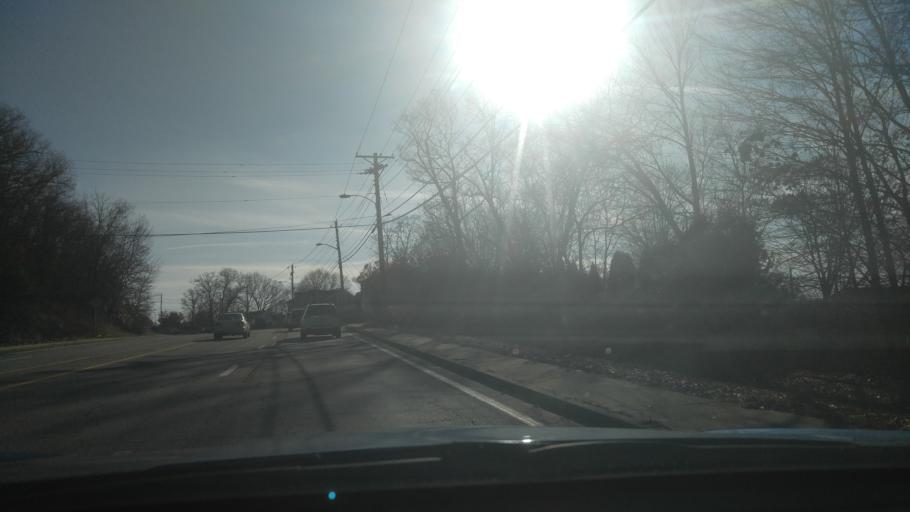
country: US
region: Rhode Island
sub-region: Providence County
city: Cumberland Hill
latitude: 41.9891
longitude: -71.4815
